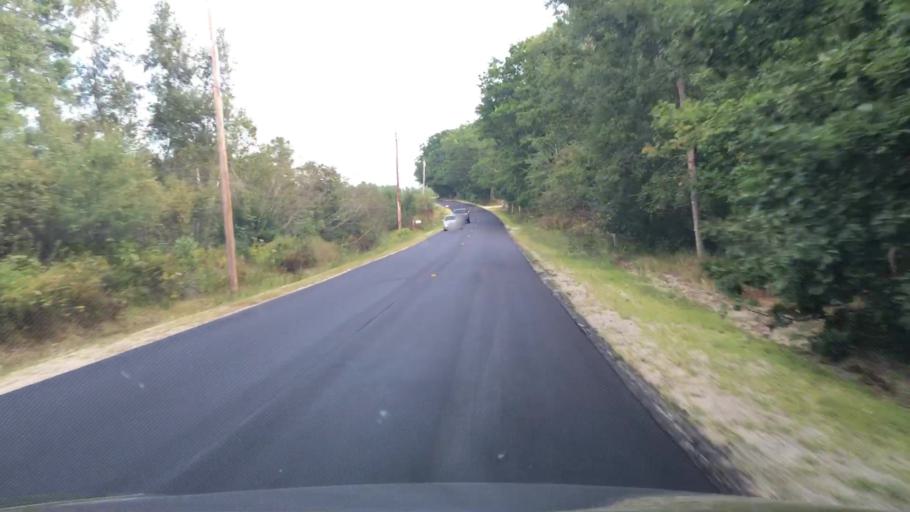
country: US
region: Maine
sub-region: Hancock County
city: Penobscot
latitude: 44.5391
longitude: -68.6157
